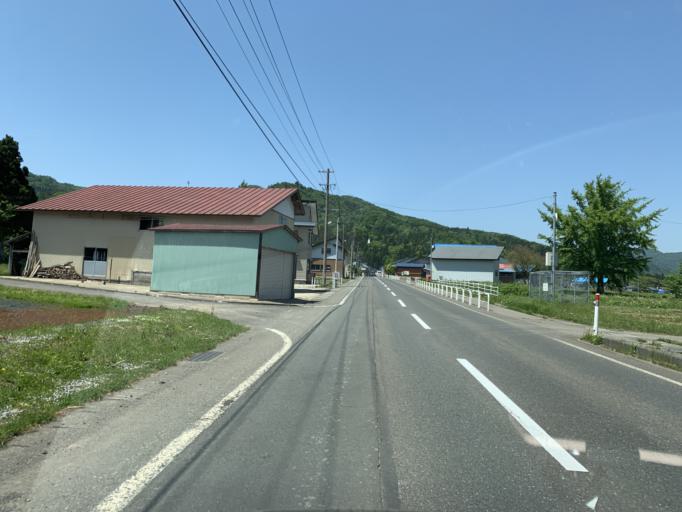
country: JP
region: Akita
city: Yokotemachi
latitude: 39.4187
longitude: 140.7466
